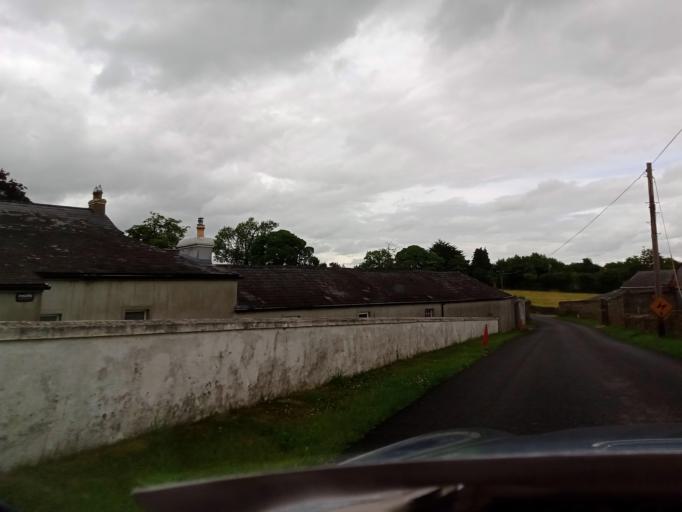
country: IE
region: Leinster
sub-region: Kilkenny
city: Thomastown
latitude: 52.5502
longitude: -7.2181
